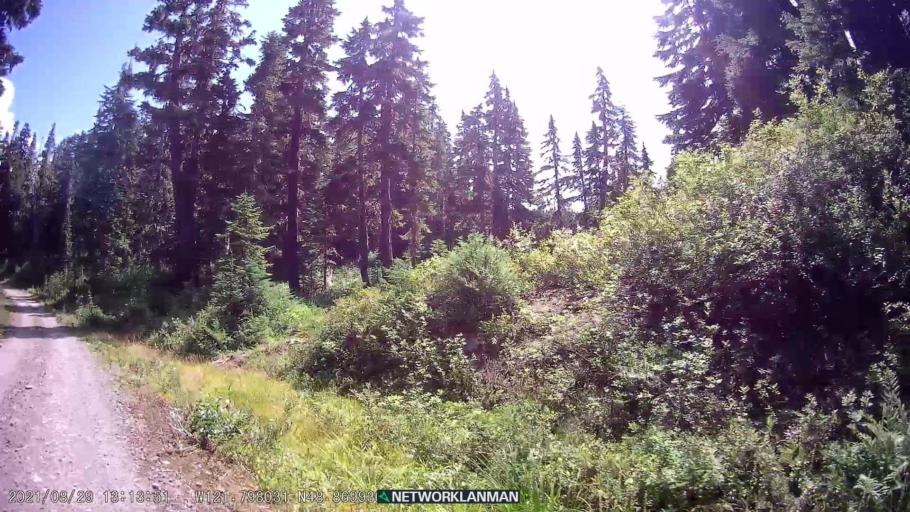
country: CA
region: British Columbia
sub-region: Fraser Valley Regional District
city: Chilliwack
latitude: 48.8700
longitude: -121.7986
